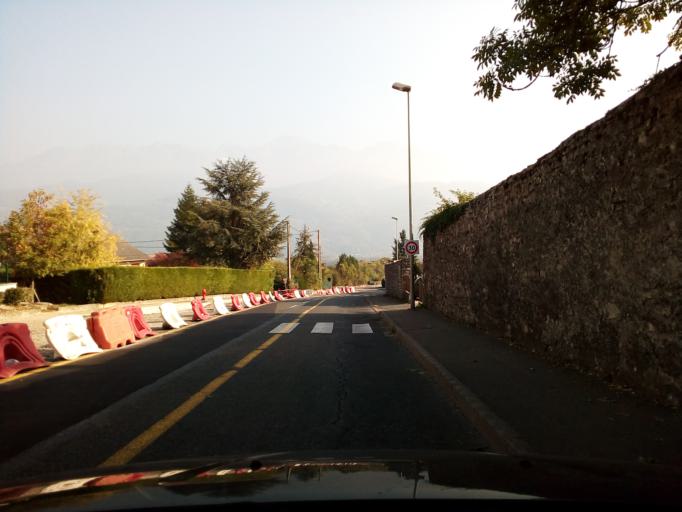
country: FR
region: Rhone-Alpes
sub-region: Departement de l'Isere
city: Saint-Ismier
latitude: 45.2428
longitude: 5.8289
